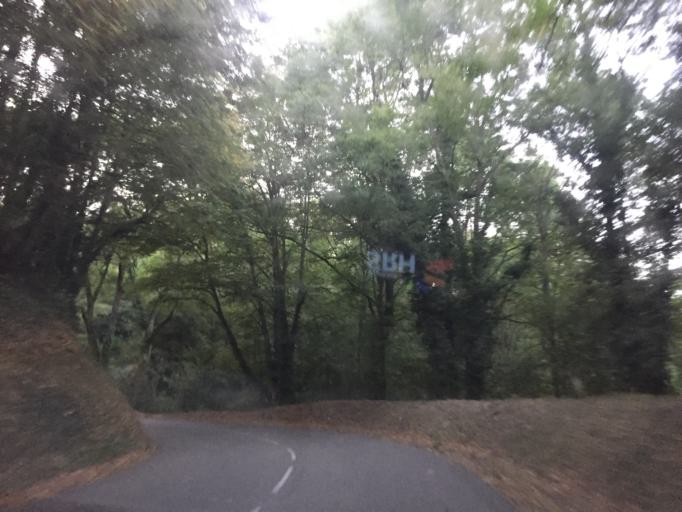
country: FR
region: Rhone-Alpes
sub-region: Departement de l'Ain
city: Saint-Maurice-de-Beynost
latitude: 45.8404
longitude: 4.9750
